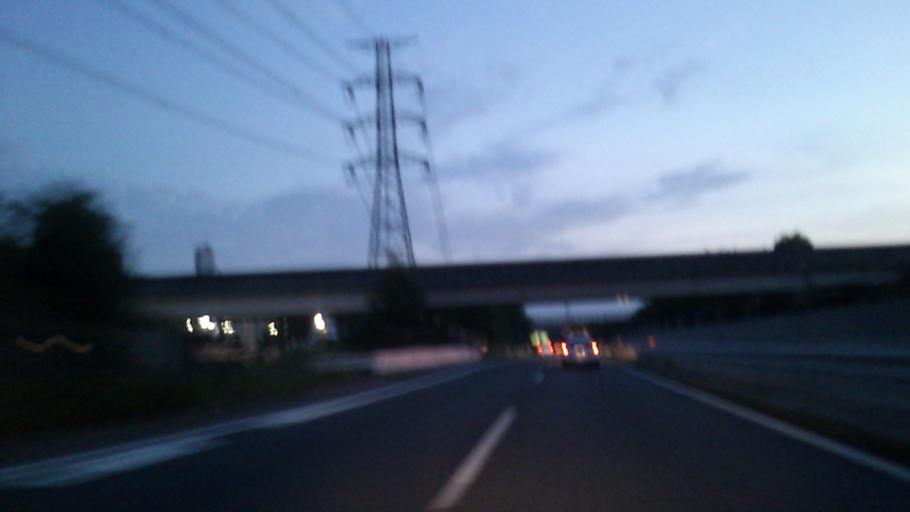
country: JP
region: Aichi
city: Kasugai
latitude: 35.2966
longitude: 136.9904
